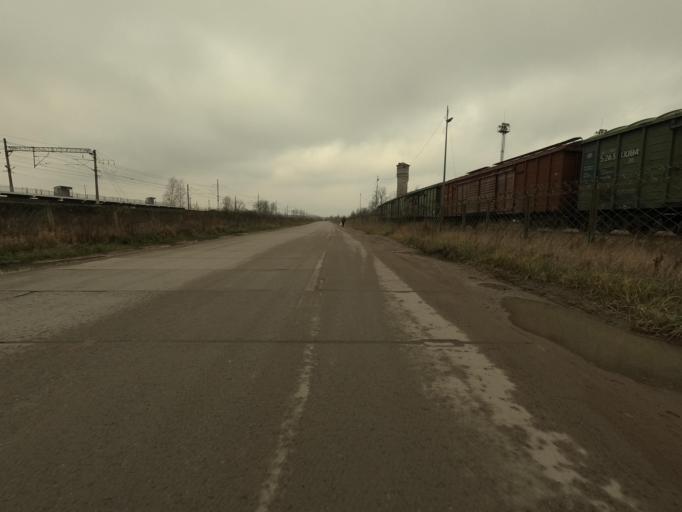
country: RU
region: Leningrad
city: Lyuban'
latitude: 59.4698
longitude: 31.2536
